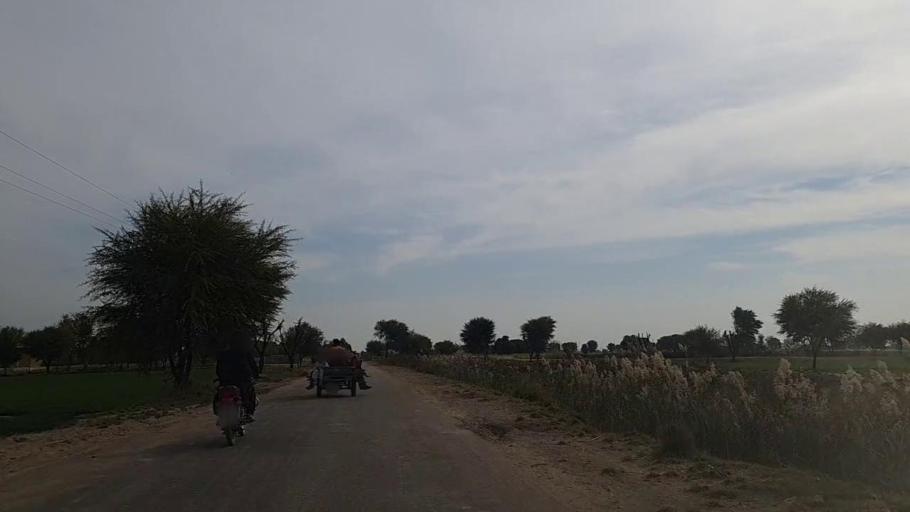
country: PK
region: Sindh
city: Daur
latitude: 26.4183
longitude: 68.4874
